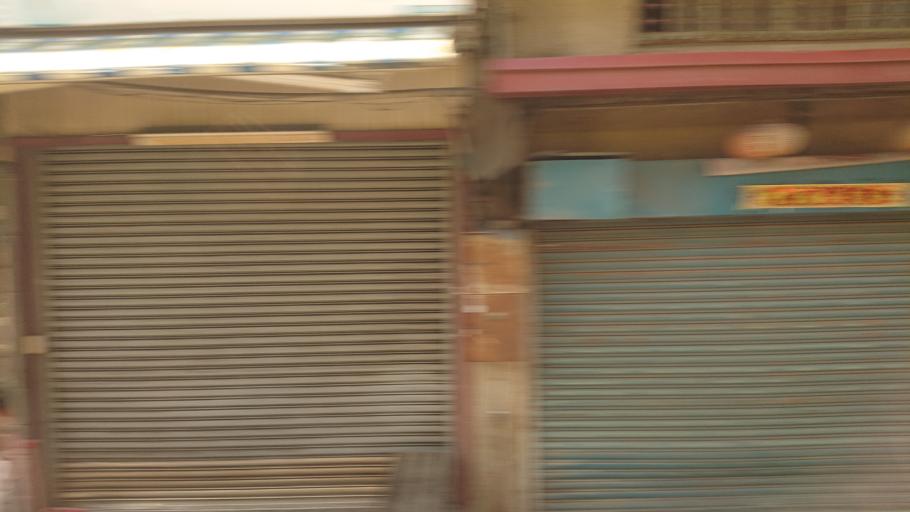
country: TW
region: Taiwan
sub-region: Nantou
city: Puli
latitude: 24.0578
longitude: 120.9126
